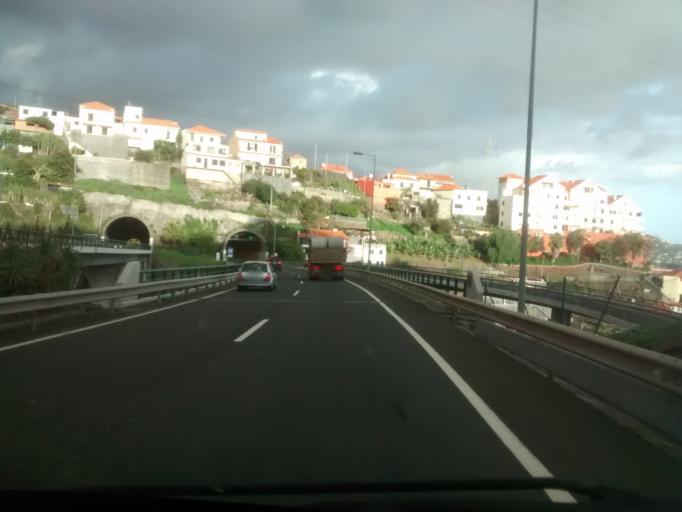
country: PT
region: Madeira
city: Camara de Lobos
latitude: 32.6595
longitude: -16.9865
